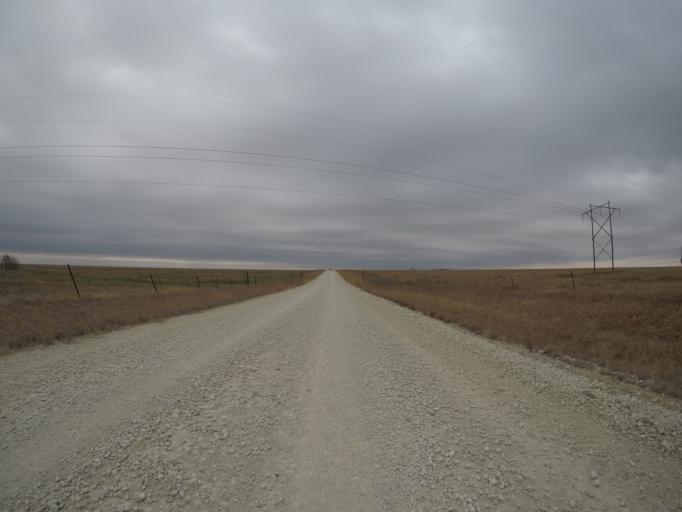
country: US
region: Kansas
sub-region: Wabaunsee County
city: Alma
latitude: 38.7544
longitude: -96.1496
